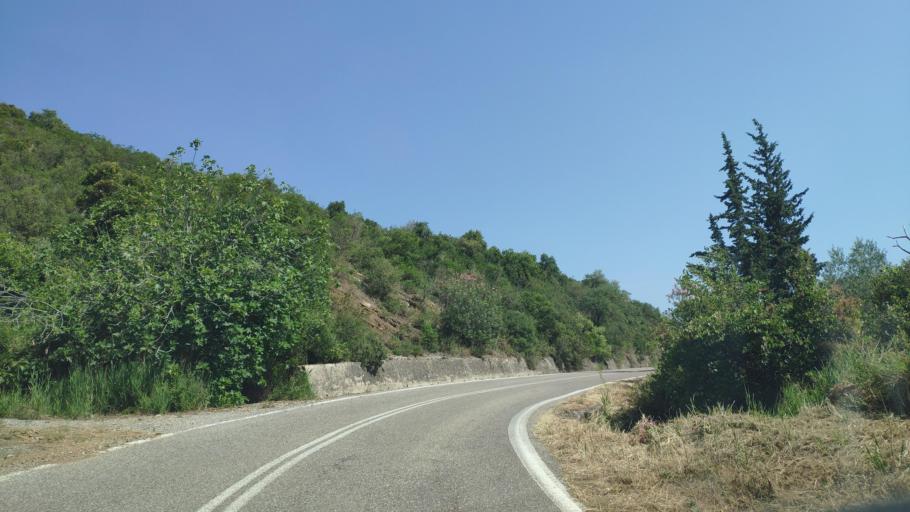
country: GR
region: West Greece
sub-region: Nomos Aitolias kai Akarnanias
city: Lepenou
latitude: 38.7608
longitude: 21.3378
